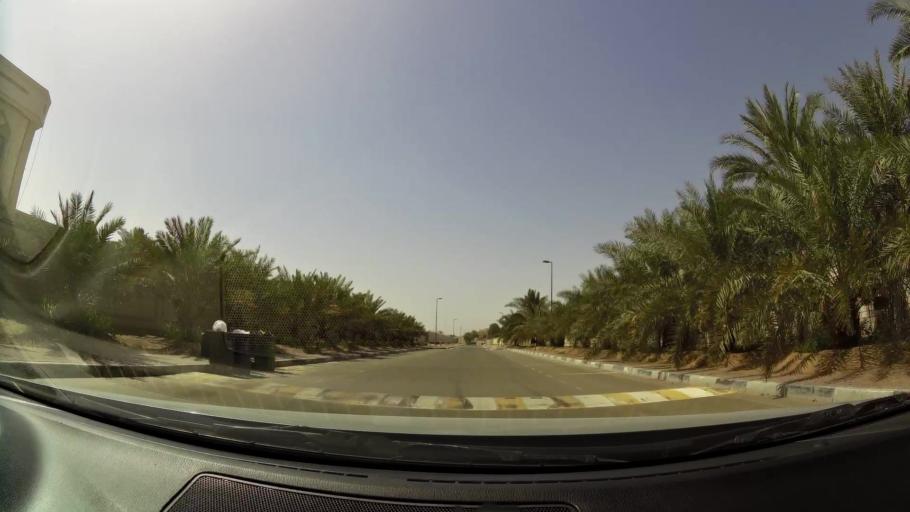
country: OM
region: Al Buraimi
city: Al Buraymi
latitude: 24.2992
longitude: 55.7606
